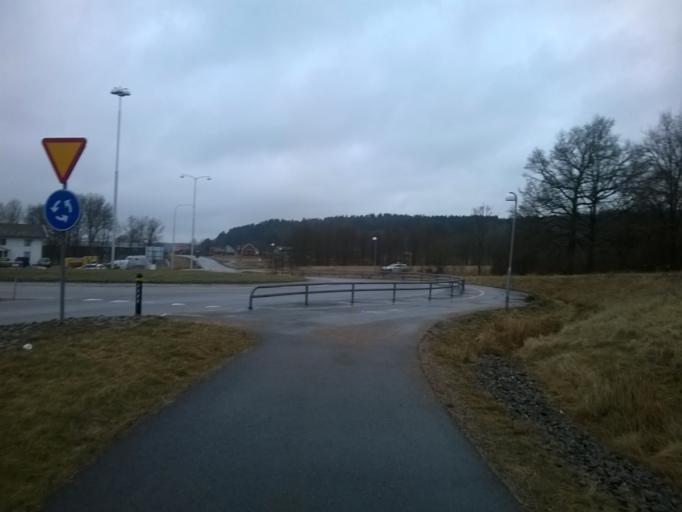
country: SE
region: Vaestra Goetaland
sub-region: Kungalvs Kommun
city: Kungalv
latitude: 57.8943
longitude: 11.9396
